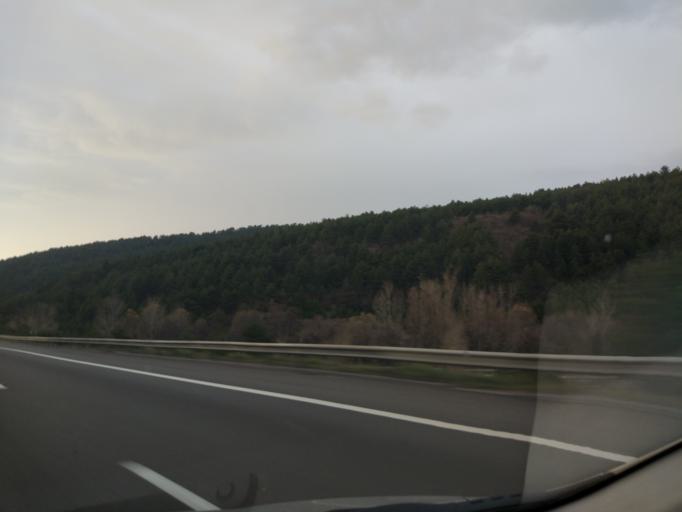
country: TR
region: Bolu
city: Gokcesu
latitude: 40.7394
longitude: 31.8309
